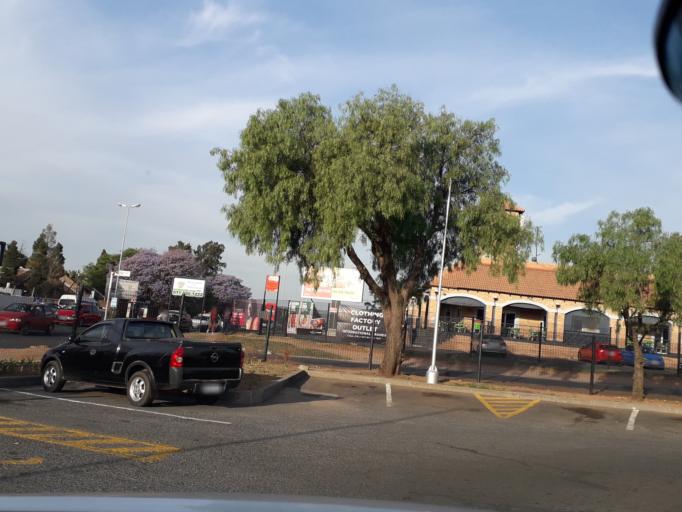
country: ZA
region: Gauteng
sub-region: City of Johannesburg Metropolitan Municipality
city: Johannesburg
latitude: -26.0933
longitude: 27.9844
